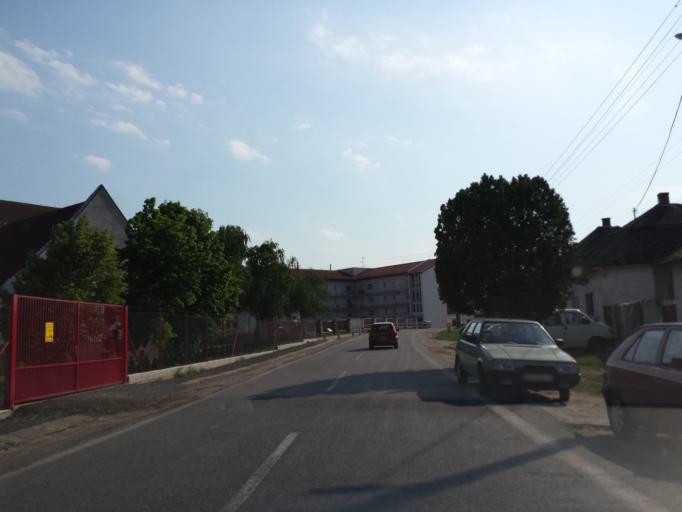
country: AT
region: Lower Austria
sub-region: Politischer Bezirk Ganserndorf
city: Angern an der March
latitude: 48.3840
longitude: 16.8575
